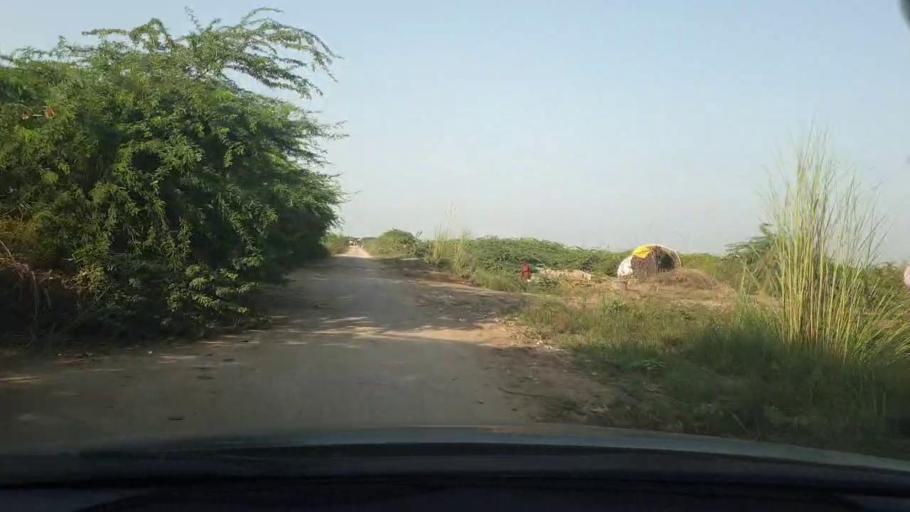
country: PK
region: Sindh
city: Naukot
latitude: 24.7725
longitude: 69.2313
